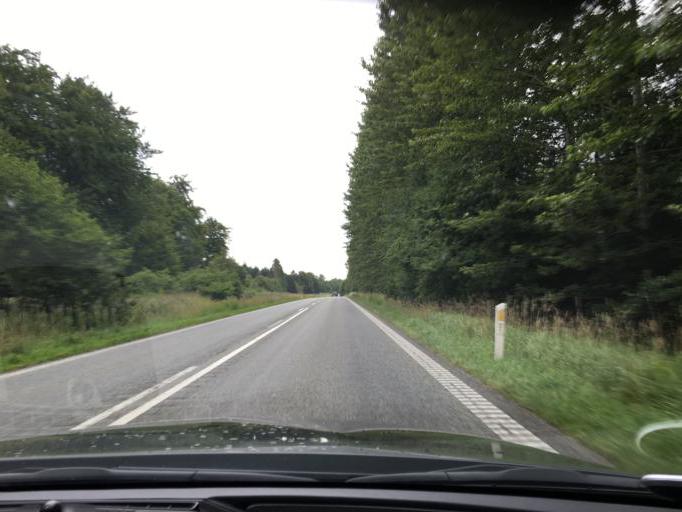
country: DK
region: Capital Region
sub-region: Allerod Kommune
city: Blovstrod
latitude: 55.9184
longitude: 12.3837
